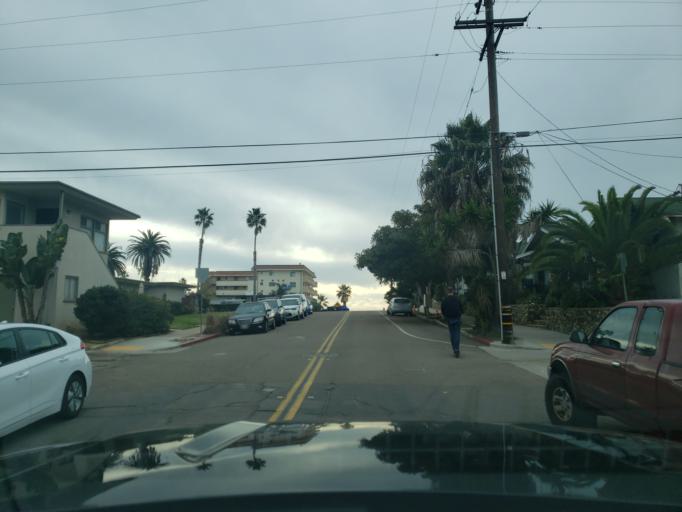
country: US
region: California
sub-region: San Diego County
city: Coronado
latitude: 32.7404
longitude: -117.2539
